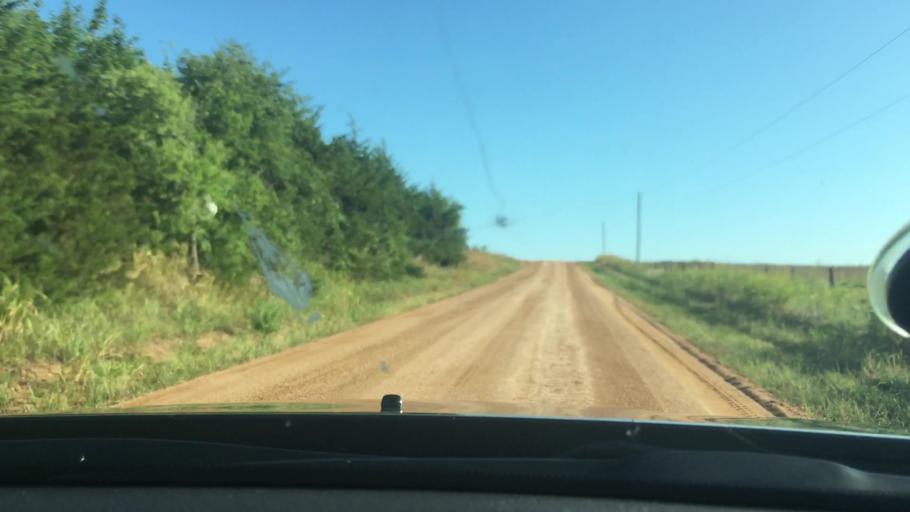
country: US
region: Oklahoma
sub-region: Murray County
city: Sulphur
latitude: 34.4088
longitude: -96.7936
